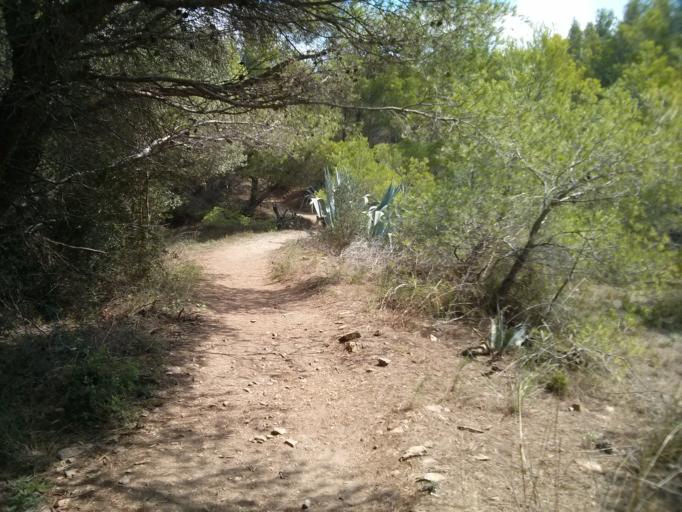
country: ES
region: Catalonia
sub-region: Provincia de Girona
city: Colera
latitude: 42.3872
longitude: 3.1604
